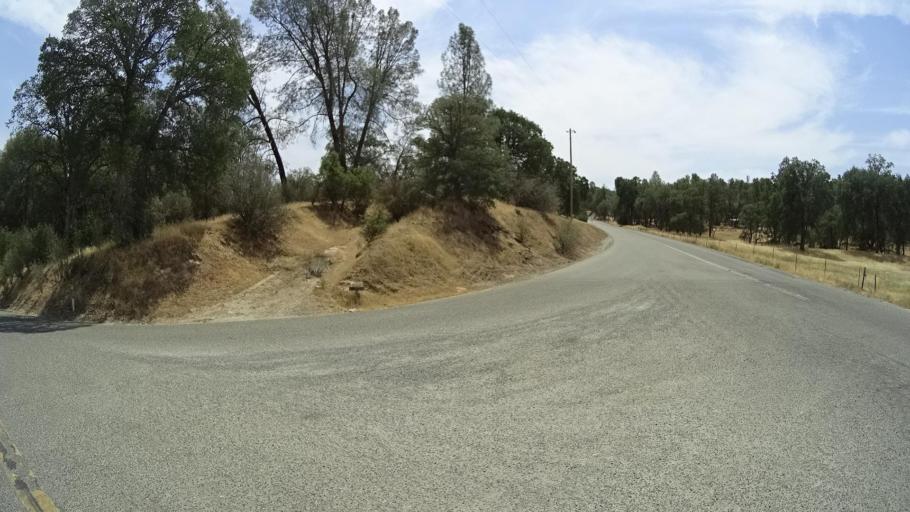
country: US
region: California
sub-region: Mariposa County
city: Mariposa
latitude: 37.4210
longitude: -119.8768
